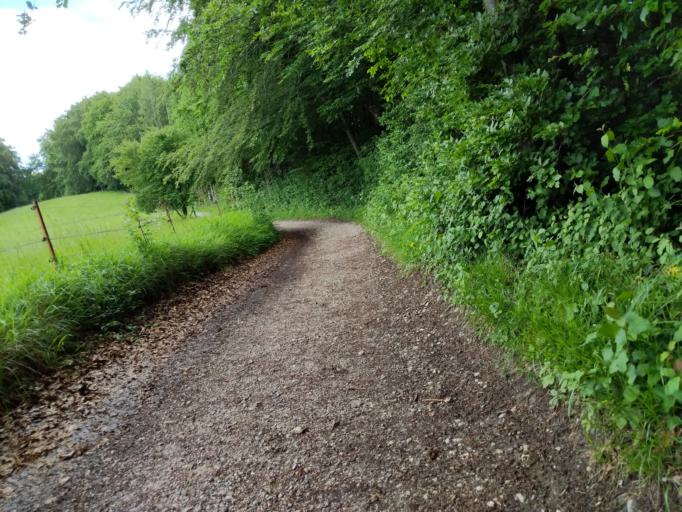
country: DE
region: Bavaria
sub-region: Upper Bavaria
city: Herrsching am Ammersee
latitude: 48.0137
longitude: 11.1931
